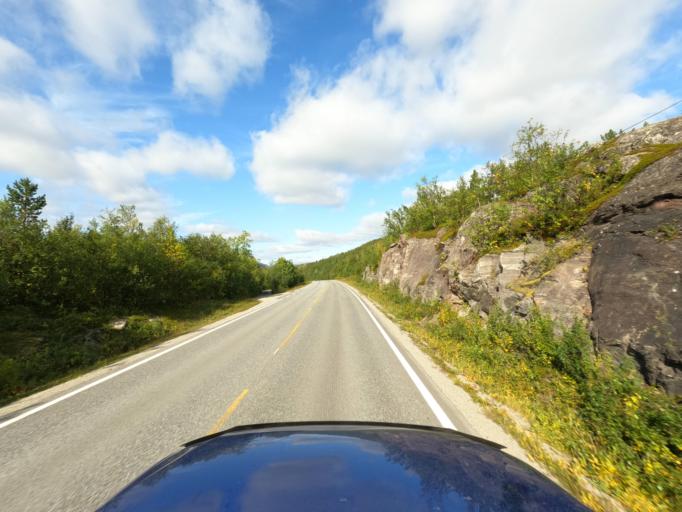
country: NO
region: Finnmark Fylke
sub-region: Porsanger
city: Lakselv
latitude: 69.9364
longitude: 24.9743
